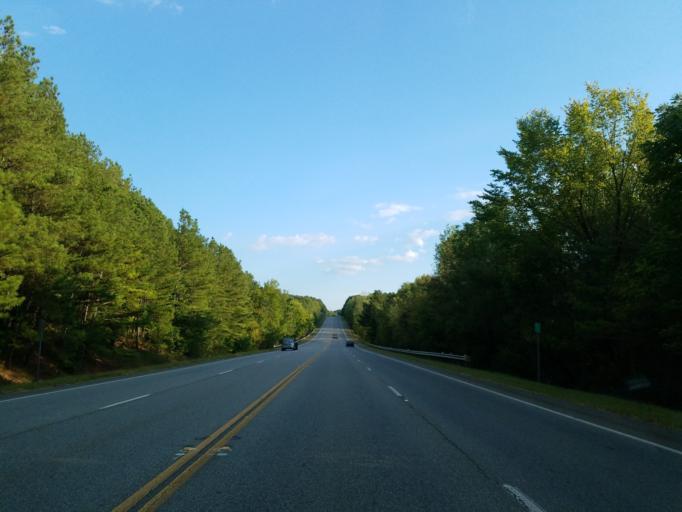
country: US
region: Georgia
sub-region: Murray County
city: Chatsworth
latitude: 34.7233
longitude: -84.7486
